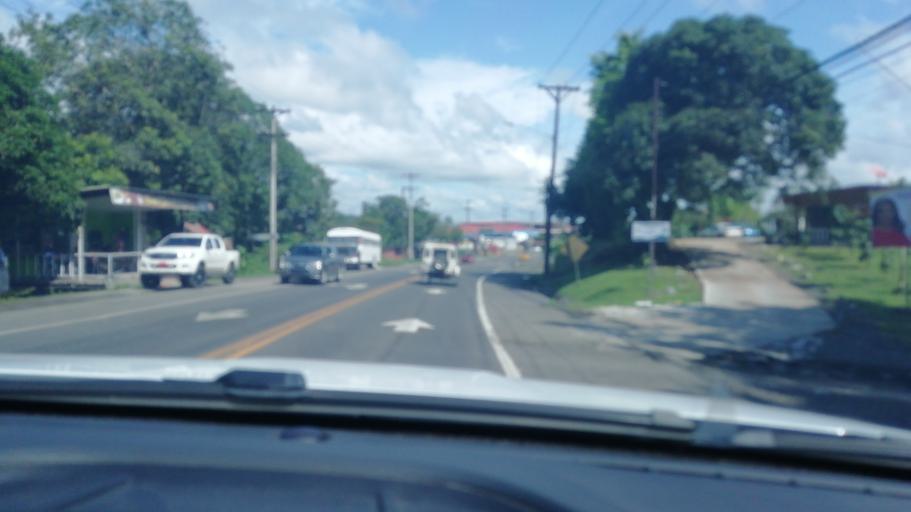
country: PA
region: Panama
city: Chilibre
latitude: 9.1360
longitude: -79.6204
